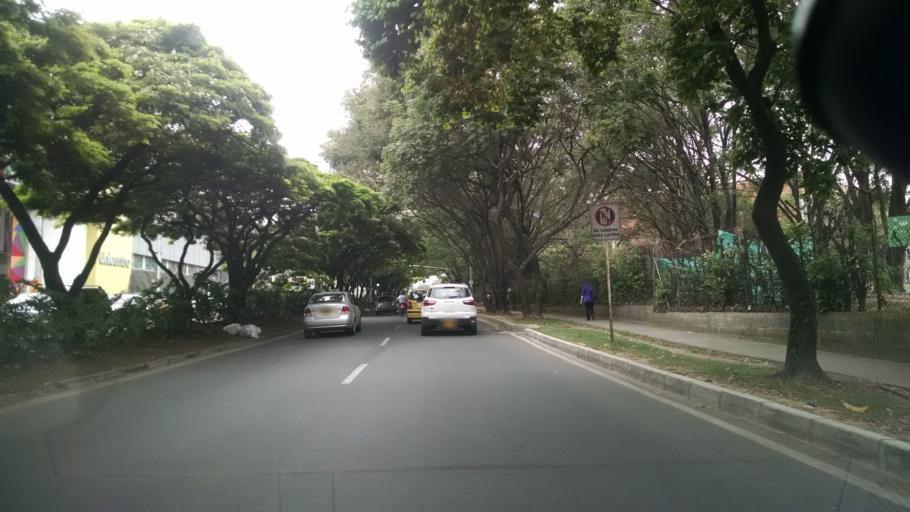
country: CO
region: Antioquia
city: Medellin
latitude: 6.2424
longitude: -75.5869
